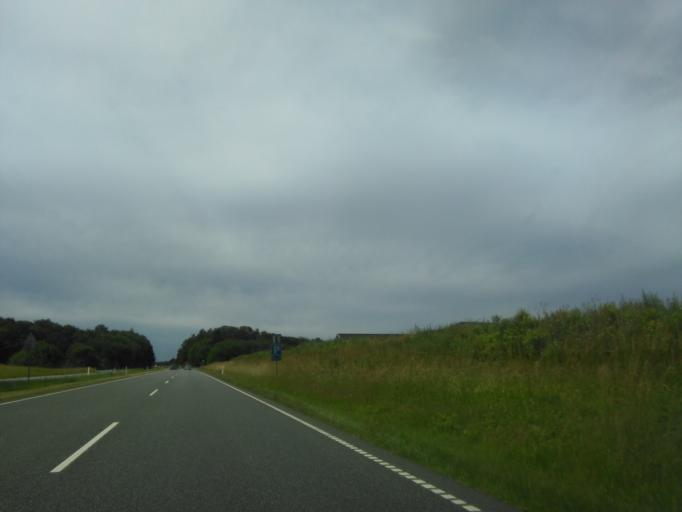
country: DK
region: Central Jutland
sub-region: Arhus Kommune
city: Tranbjerg
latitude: 56.0830
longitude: 10.1192
